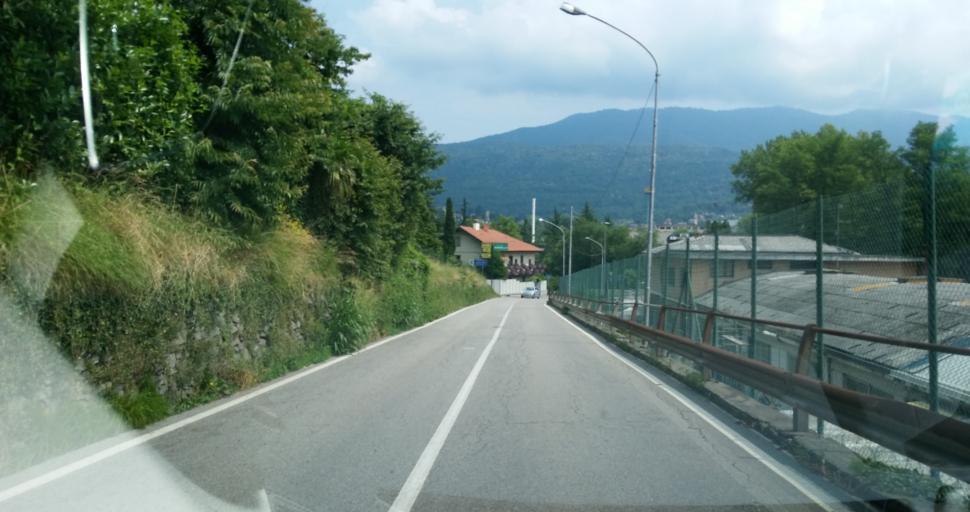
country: IT
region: Lombardy
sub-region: Provincia di Varese
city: Bardello
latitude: 45.8357
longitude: 8.7006
